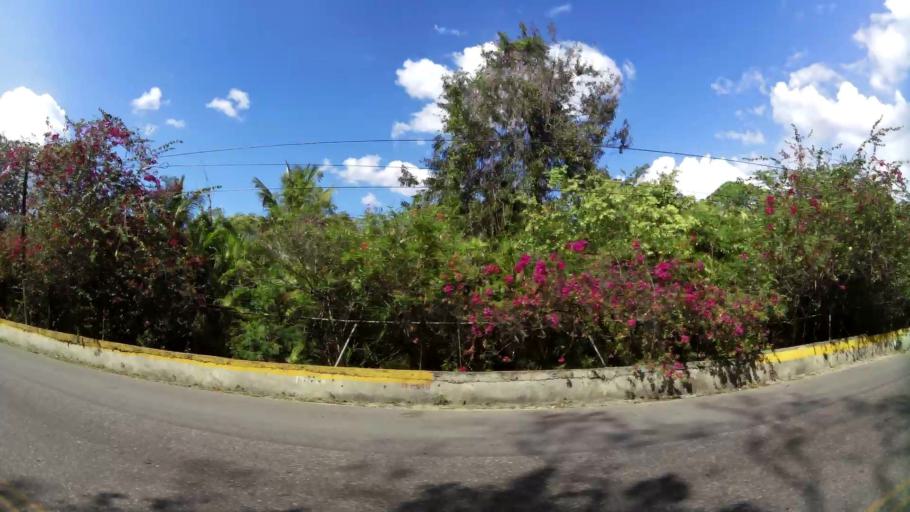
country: DO
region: San Cristobal
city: Bajos de Haina
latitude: 18.4266
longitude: -70.0568
